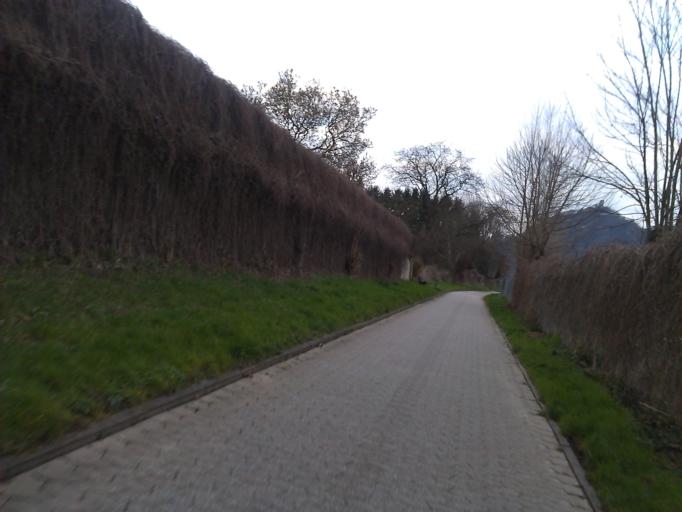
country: DE
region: North Rhine-Westphalia
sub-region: Regierungsbezirk Koln
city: Bad Honnef
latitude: 50.6469
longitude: 7.2063
